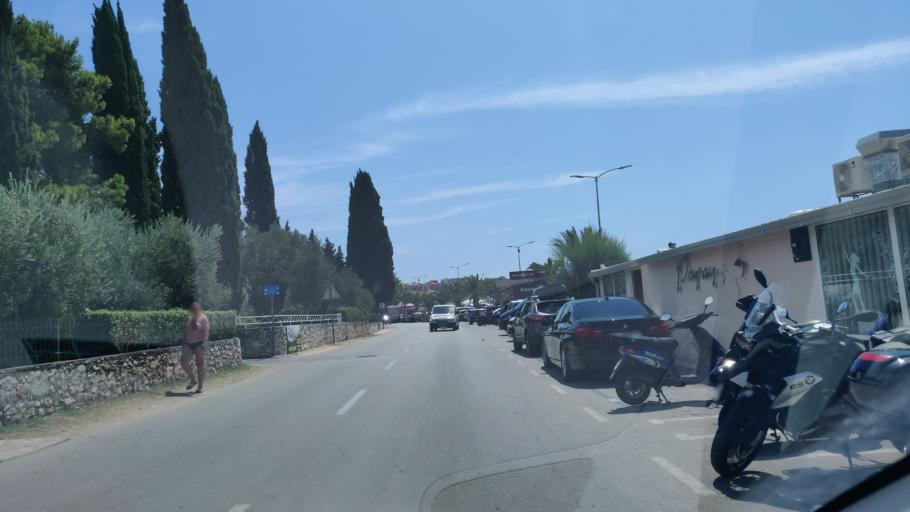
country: HR
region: Splitsko-Dalmatinska
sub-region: Grad Trogir
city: Trogir
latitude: 43.5010
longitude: 16.2592
